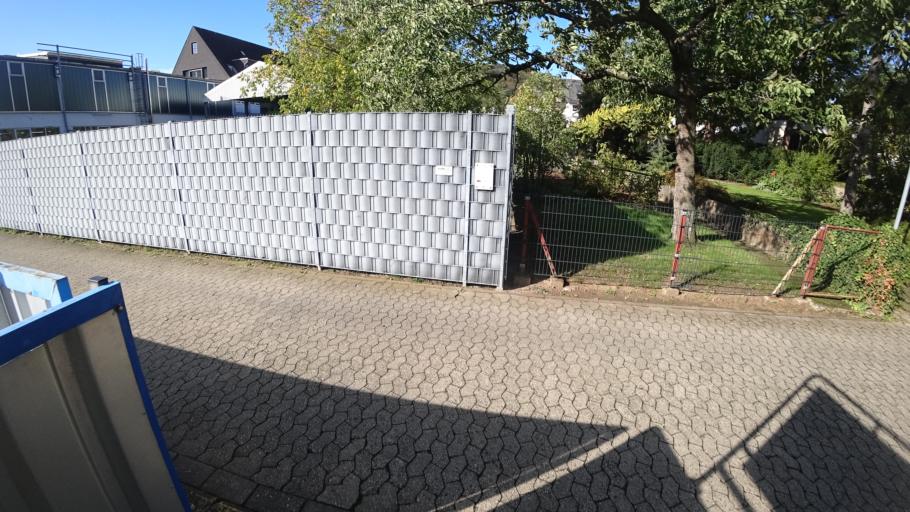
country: DE
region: Rheinland-Pfalz
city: Spay
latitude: 50.2578
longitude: 7.6503
